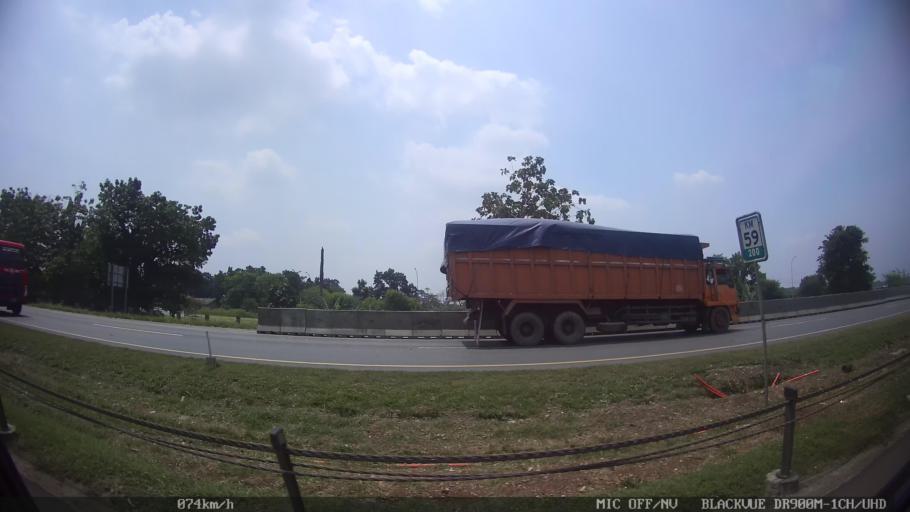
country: ID
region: West Java
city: Kresek
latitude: -6.1442
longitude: 106.2913
